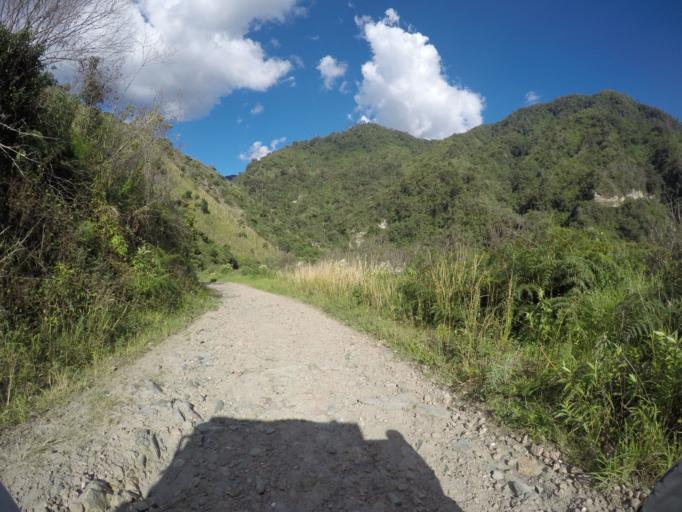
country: CO
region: Tolima
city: Cajamarca
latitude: 4.5055
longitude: -75.3955
